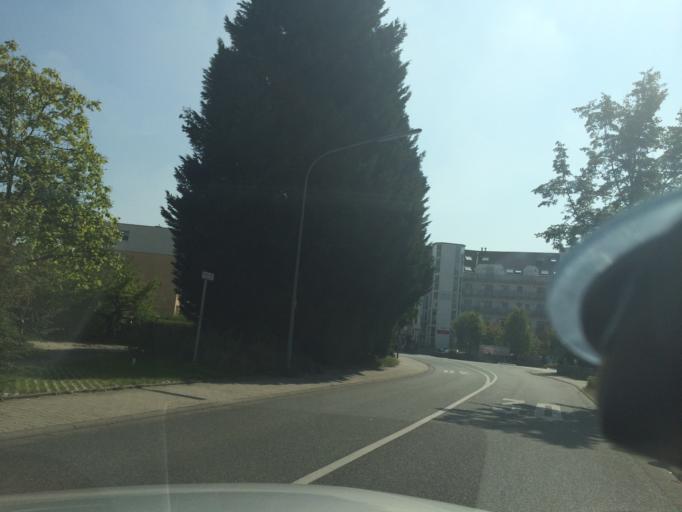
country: DE
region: Hesse
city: Morfelden-Walldorf
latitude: 49.9802
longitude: 8.5624
